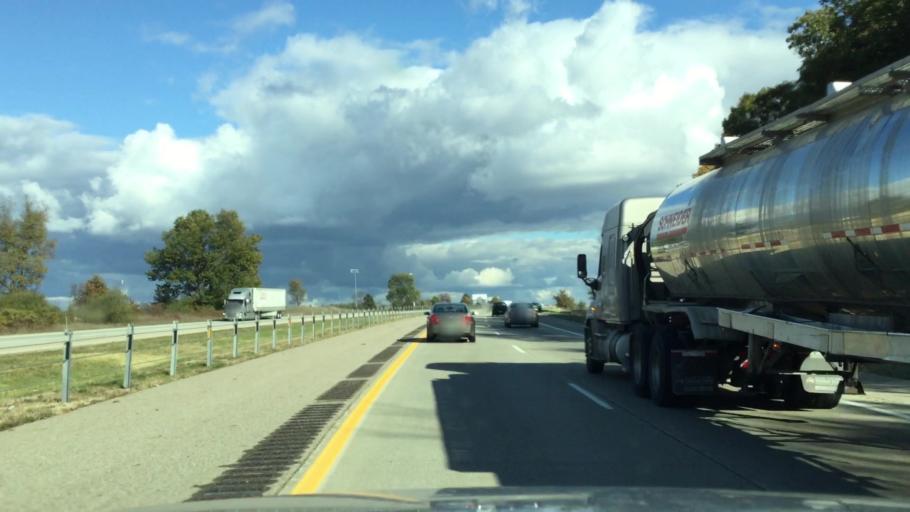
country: US
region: Michigan
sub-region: Van Buren County
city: Paw Paw
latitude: 42.2168
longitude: -85.8556
